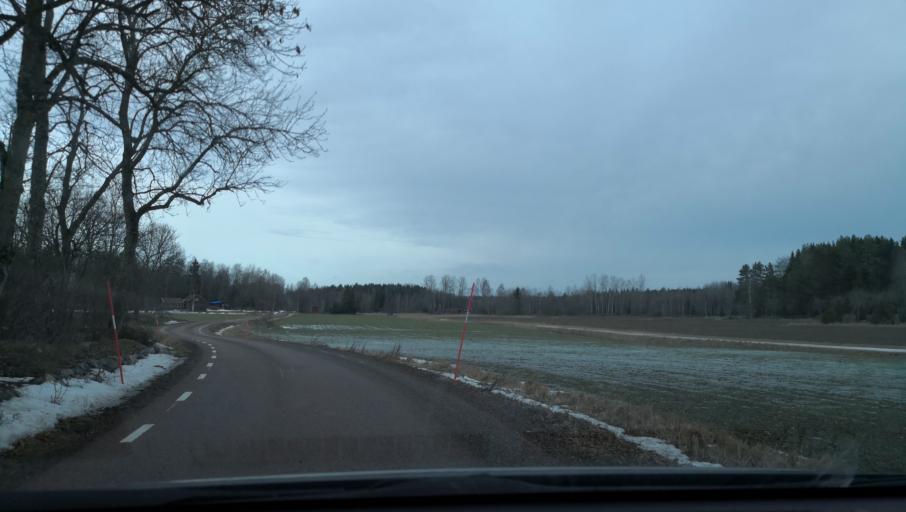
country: SE
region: Vaestmanland
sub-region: Vasteras
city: Skultuna
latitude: 59.6217
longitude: 16.4133
